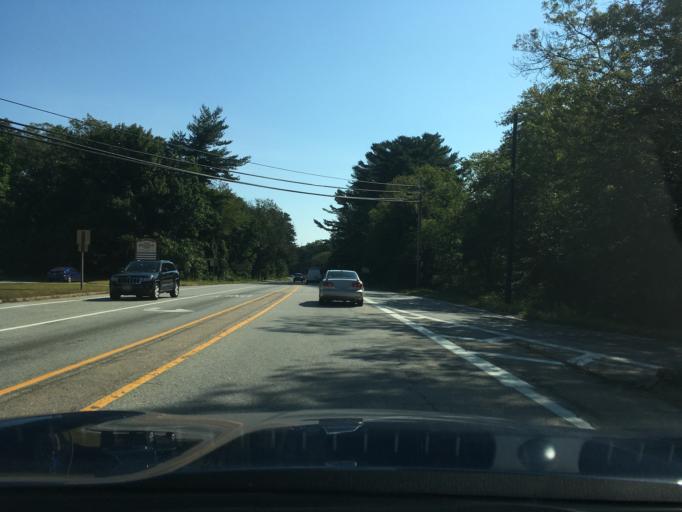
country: US
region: Rhode Island
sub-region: Washington County
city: Exeter
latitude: 41.5762
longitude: -71.5158
